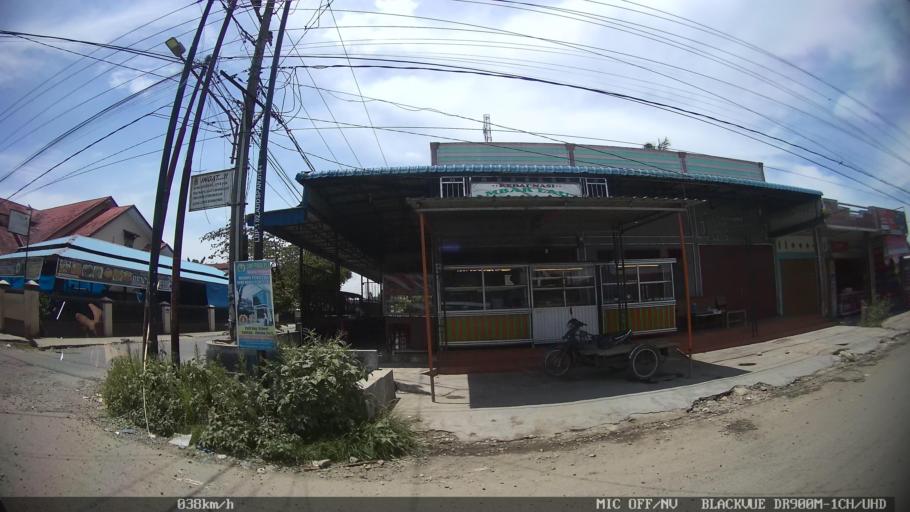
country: ID
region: North Sumatra
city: Binjai
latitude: 3.5912
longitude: 98.5021
